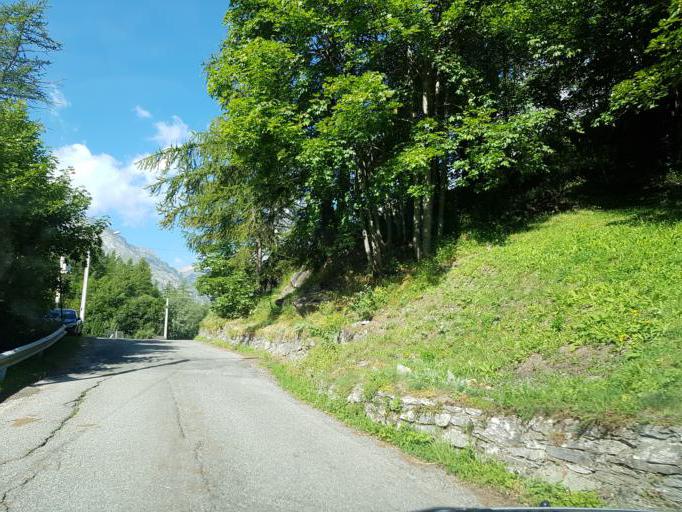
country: IT
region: Piedmont
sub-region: Provincia di Cuneo
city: Pleyne
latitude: 44.5806
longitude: 7.0157
